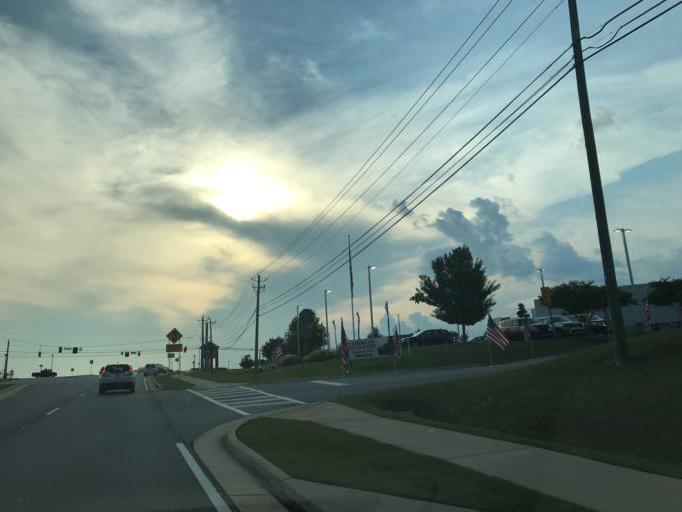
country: US
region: Alabama
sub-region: Russell County
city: Phenix City
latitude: 32.5395
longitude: -84.9645
